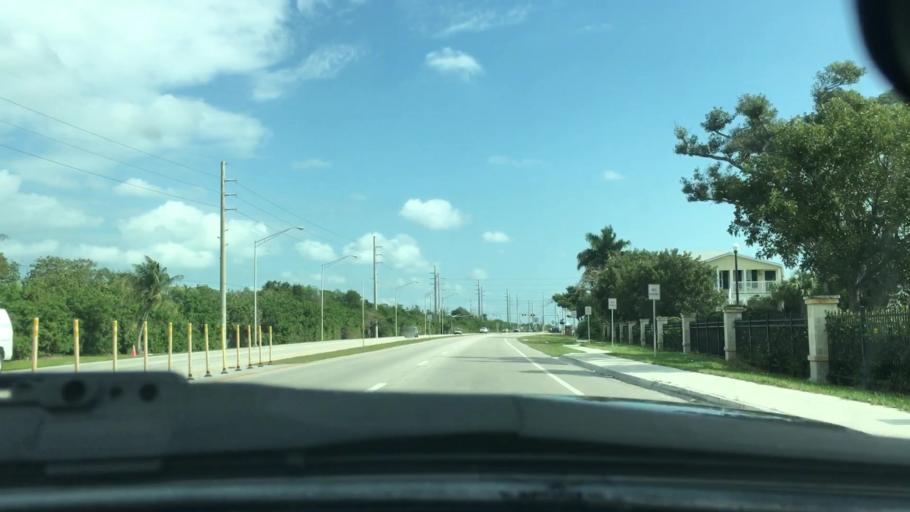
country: US
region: Florida
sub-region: Monroe County
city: Stock Island
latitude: 24.5737
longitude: -81.7402
